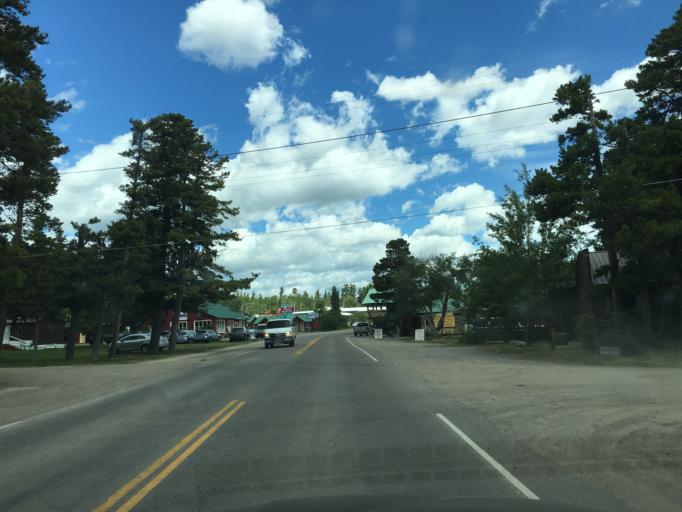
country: US
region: Montana
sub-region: Glacier County
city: South Browning
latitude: 48.4477
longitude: -113.2249
